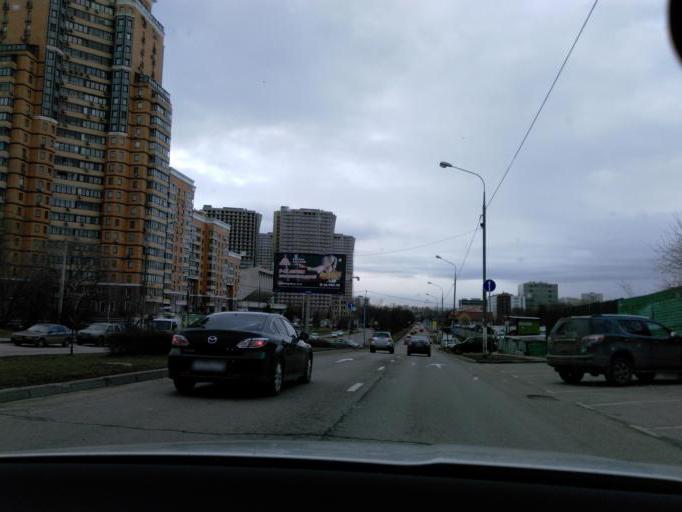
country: RU
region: Moscow
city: Golovinskiy
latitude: 55.8576
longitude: 37.4906
